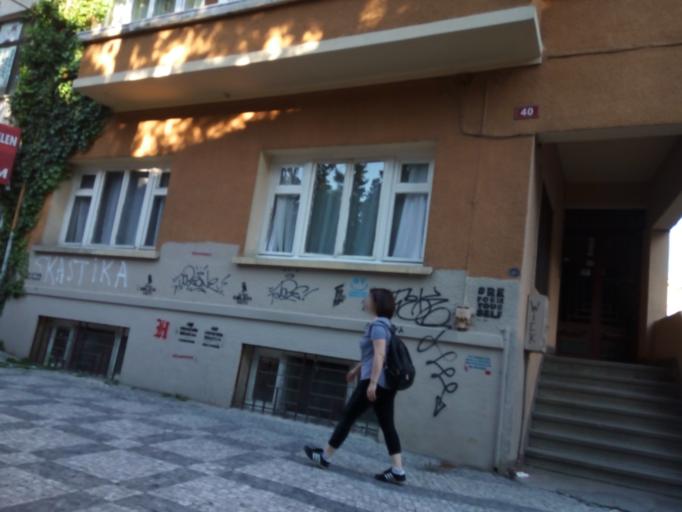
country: TR
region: Istanbul
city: UEskuedar
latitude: 40.9928
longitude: 29.0298
